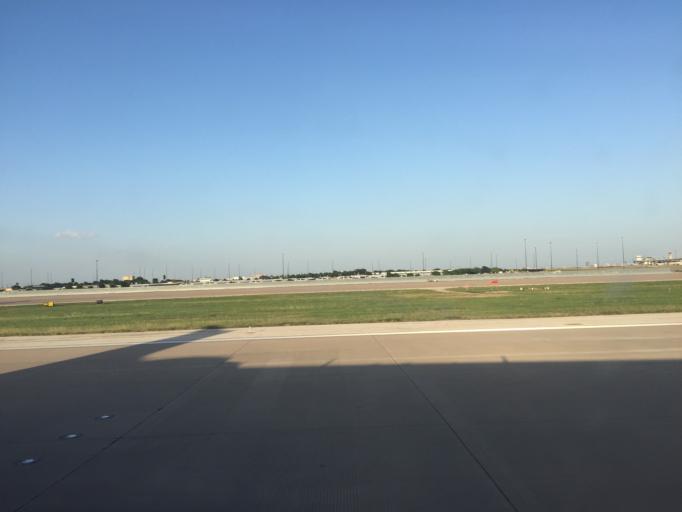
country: US
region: Texas
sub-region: Tarrant County
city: Grapevine
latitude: 32.9133
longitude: -97.0509
